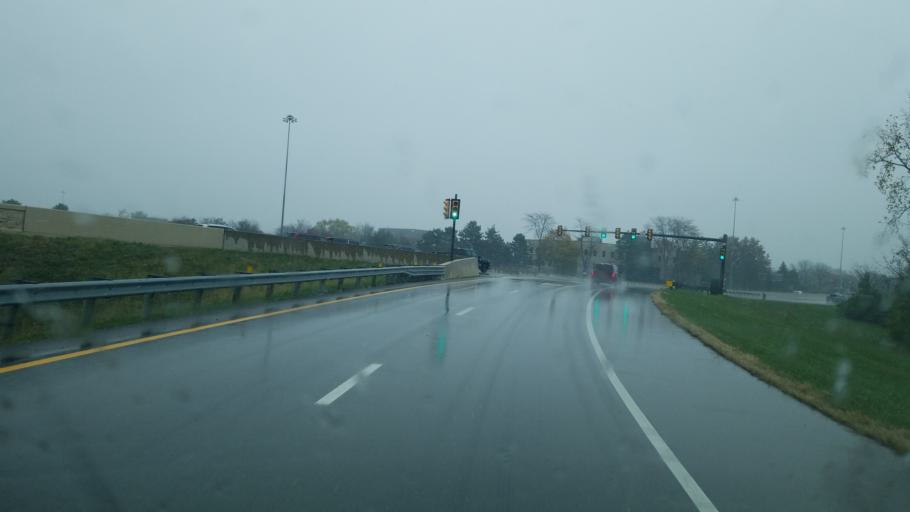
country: US
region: Ohio
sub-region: Franklin County
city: Dublin
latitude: 40.0986
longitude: -83.1318
